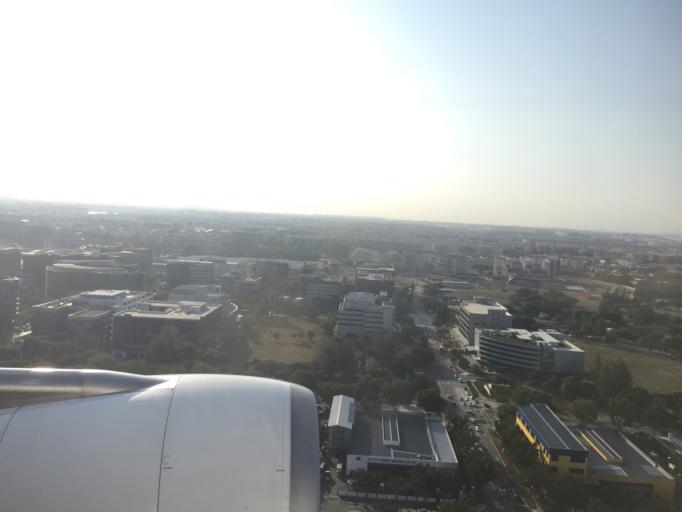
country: SG
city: Singapore
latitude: 1.3341
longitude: 103.9709
